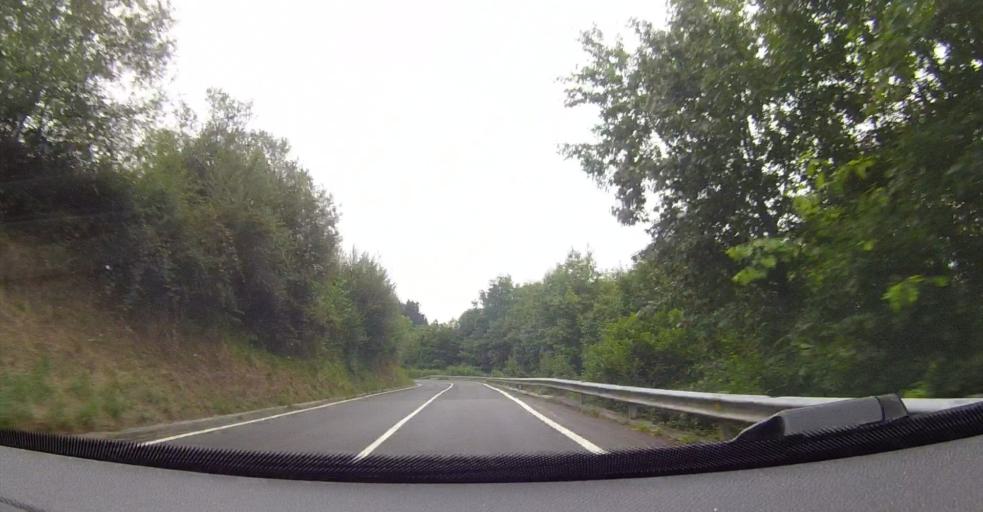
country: ES
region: Basque Country
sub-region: Bizkaia
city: Balmaseda
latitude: 43.2414
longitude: -3.2972
